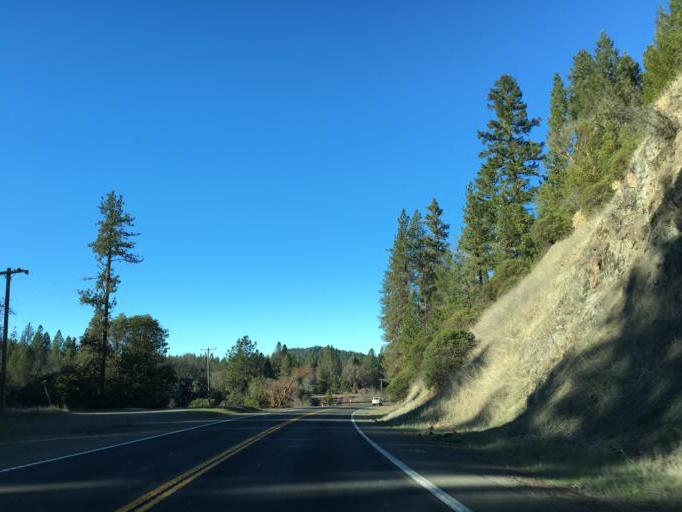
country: US
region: California
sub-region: Mendocino County
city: Laytonville
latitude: 39.7338
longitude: -123.5127
